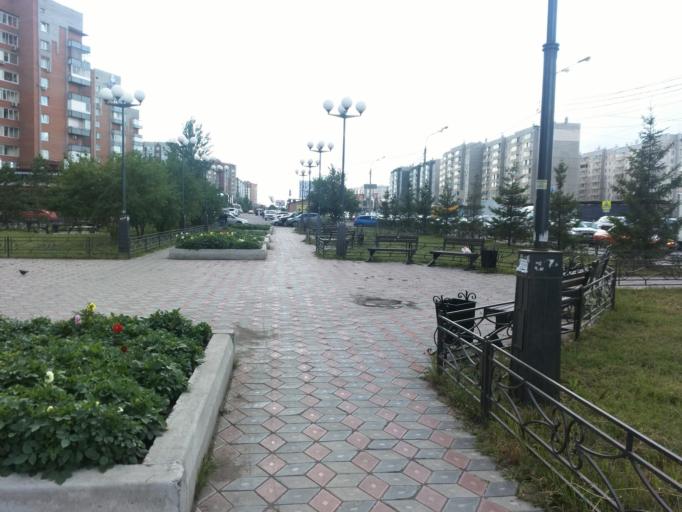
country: RU
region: Krasnoyarskiy
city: Krasnoyarsk
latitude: 56.0430
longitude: 92.9088
